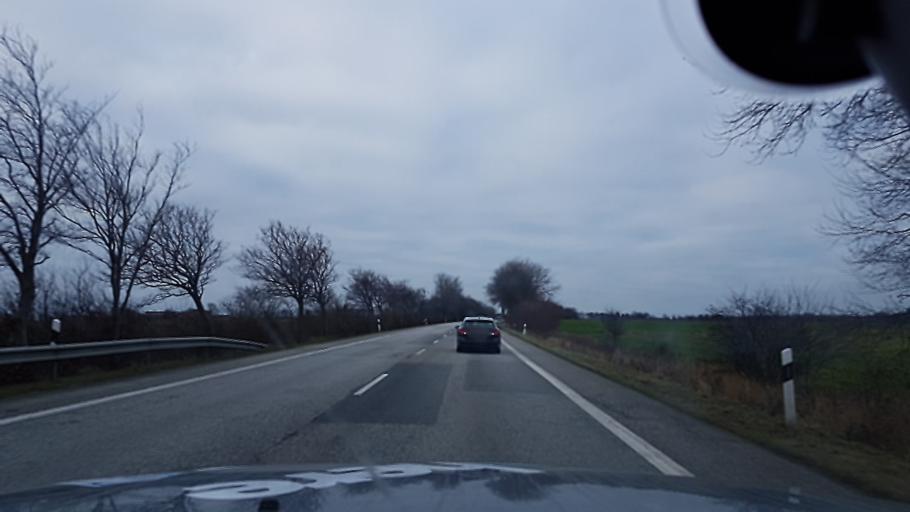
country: DE
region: Schleswig-Holstein
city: Fehmarn
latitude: 54.4504
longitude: 11.1812
